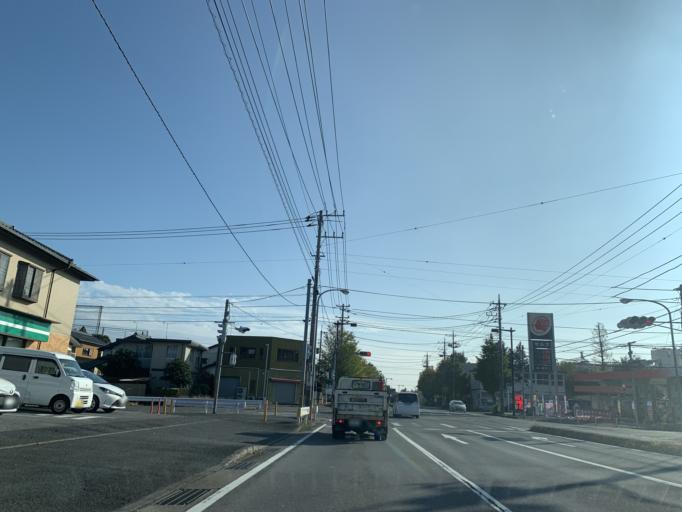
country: JP
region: Chiba
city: Nagareyama
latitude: 35.8633
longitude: 139.9118
